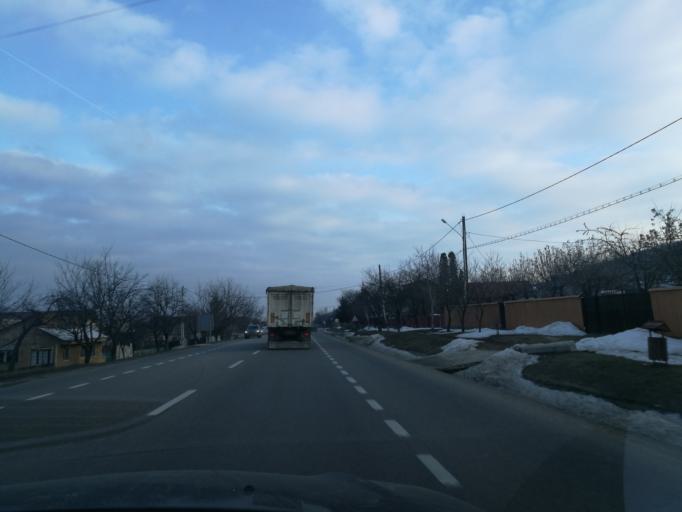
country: RO
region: Bacau
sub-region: Comuna Racaciuni
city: Gheorghe Doja
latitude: 46.3800
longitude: 26.9630
